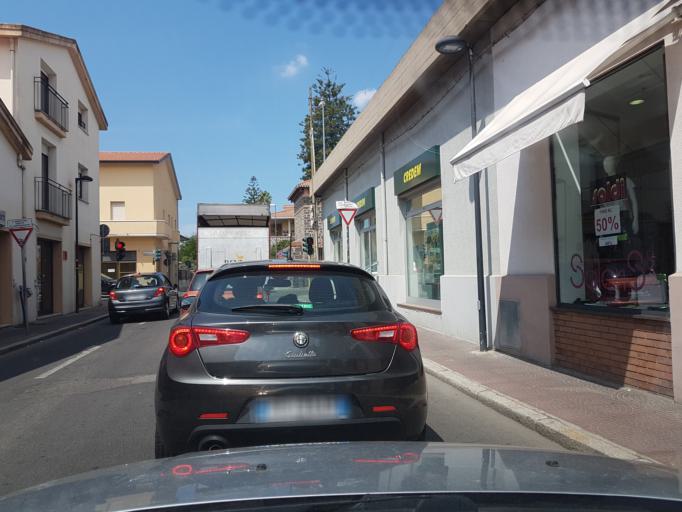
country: IT
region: Sardinia
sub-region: Provincia di Oristano
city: Oristano
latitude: 39.9060
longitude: 8.5888
